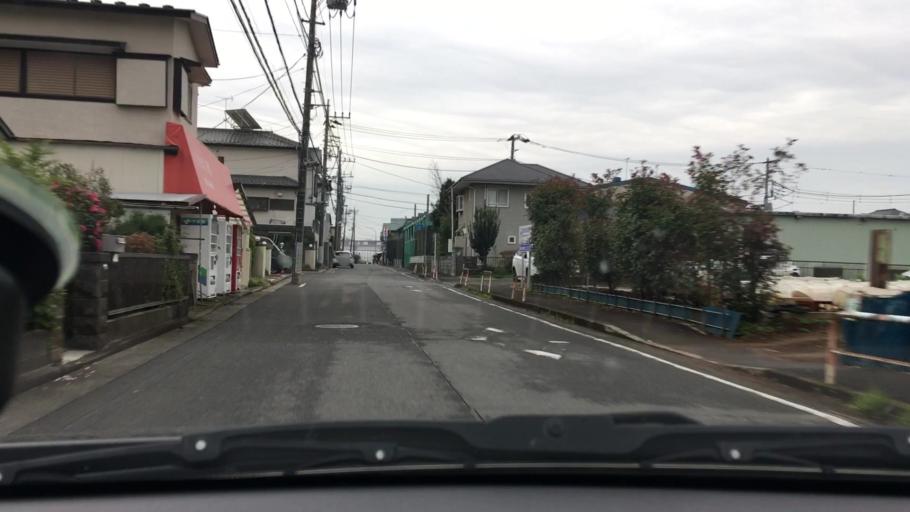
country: JP
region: Kanagawa
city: Yokohama
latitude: 35.5189
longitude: 139.6046
